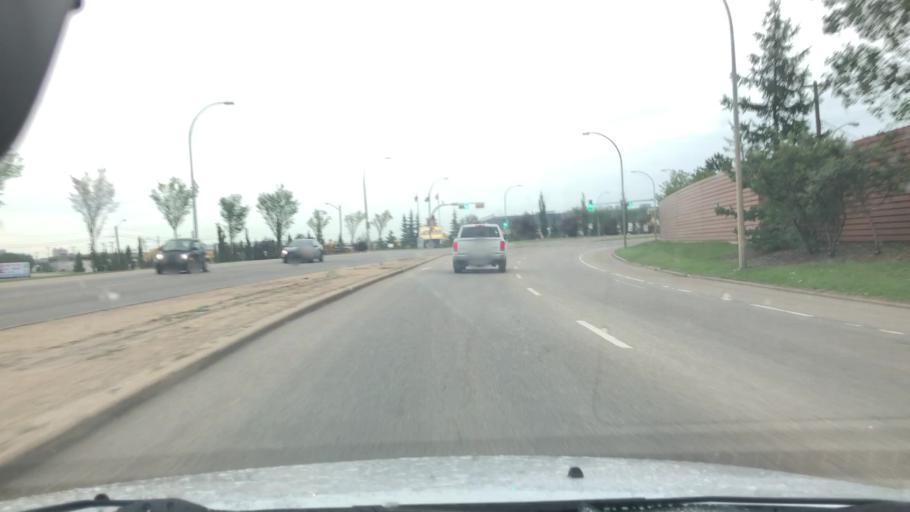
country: CA
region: Alberta
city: St. Albert
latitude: 53.5577
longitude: -113.6036
